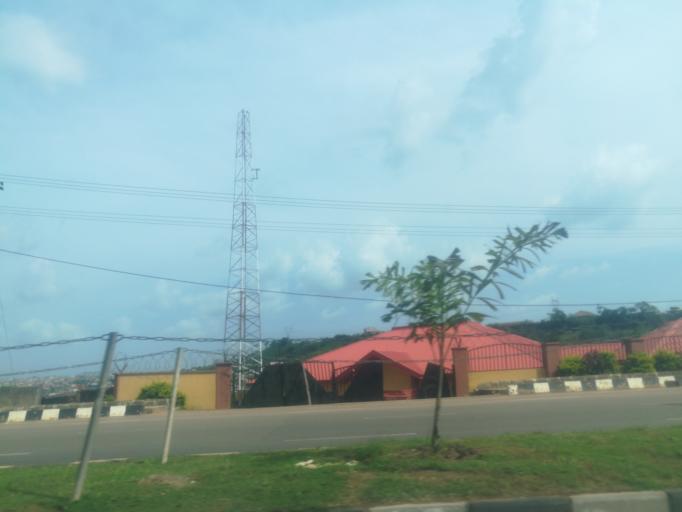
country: NG
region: Ogun
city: Abeokuta
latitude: 7.1329
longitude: 3.3657
